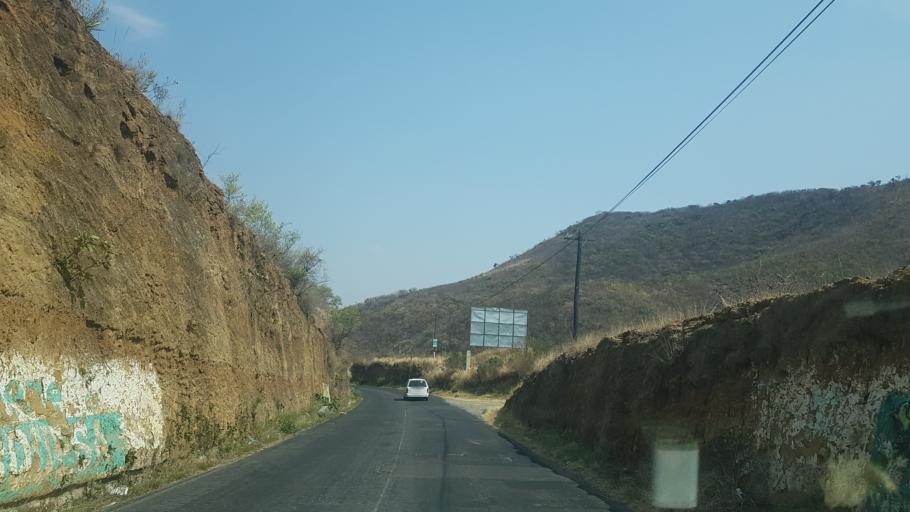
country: MX
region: Puebla
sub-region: Tianguismanalco
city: San Martin Tlapala
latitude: 18.9484
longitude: -98.4599
